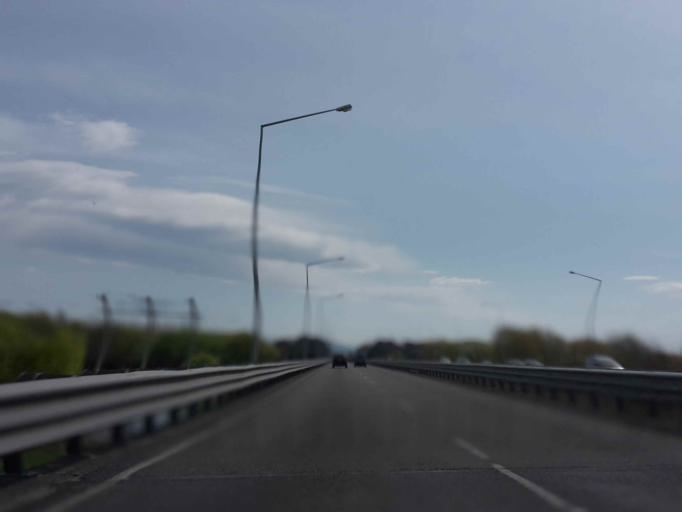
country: NZ
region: Canterbury
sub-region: Waimakariri District
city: Kaiapoi
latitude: -43.4168
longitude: 172.6471
